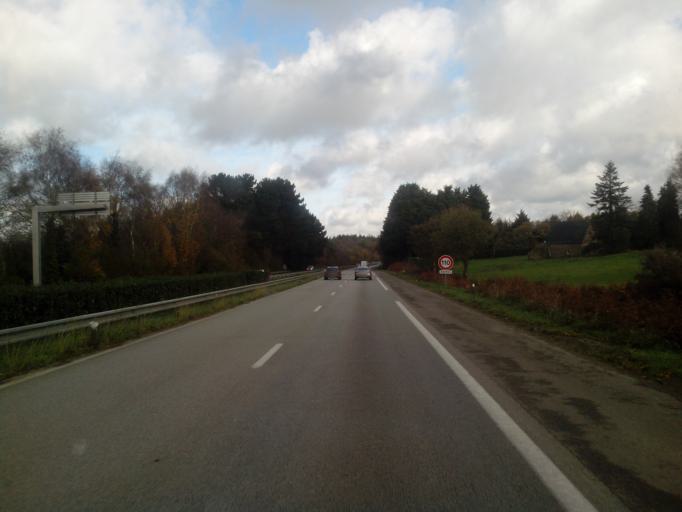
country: FR
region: Brittany
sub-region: Departement du Morbihan
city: Branderion
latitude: 47.8180
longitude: -3.2173
